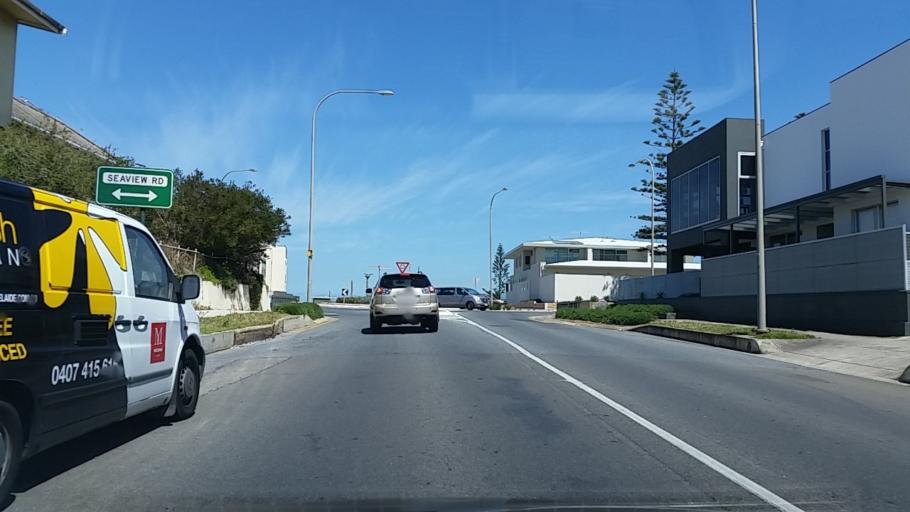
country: AU
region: South Australia
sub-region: Charles Sturt
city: Grange
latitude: -34.9075
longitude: 138.4917
